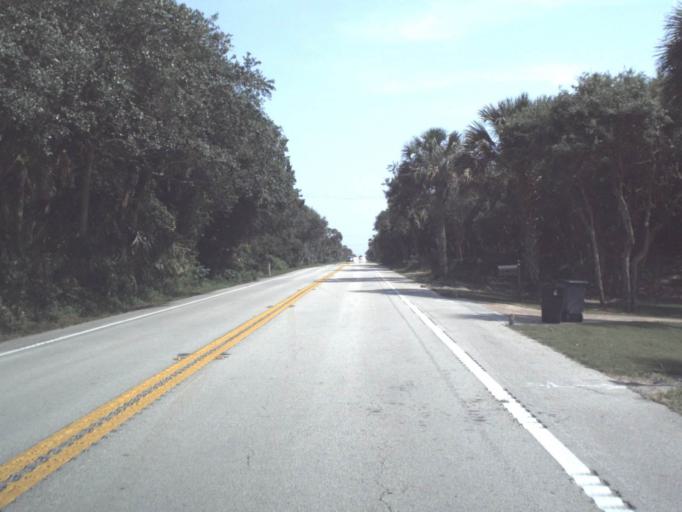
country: US
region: Florida
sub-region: Saint Johns County
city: Palm Valley
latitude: 30.1311
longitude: -81.3494
